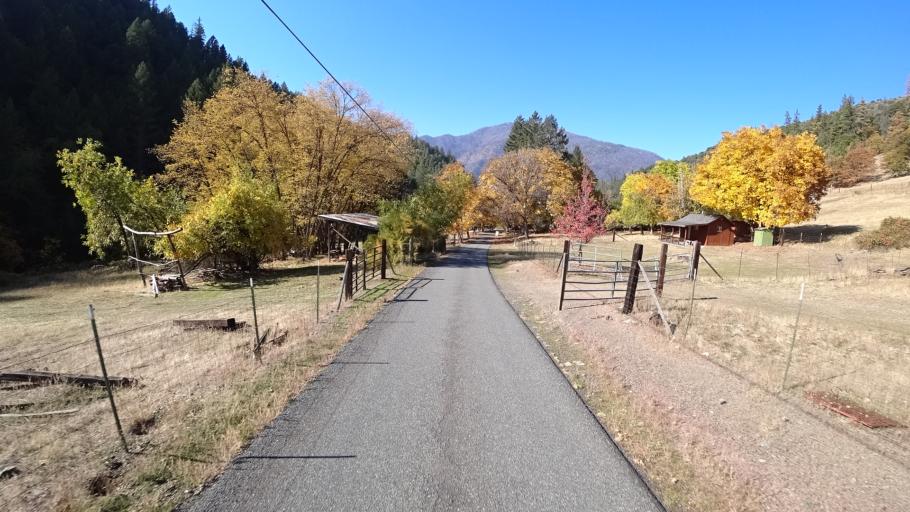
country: US
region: California
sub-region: Siskiyou County
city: Yreka
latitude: 41.7420
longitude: -122.9834
